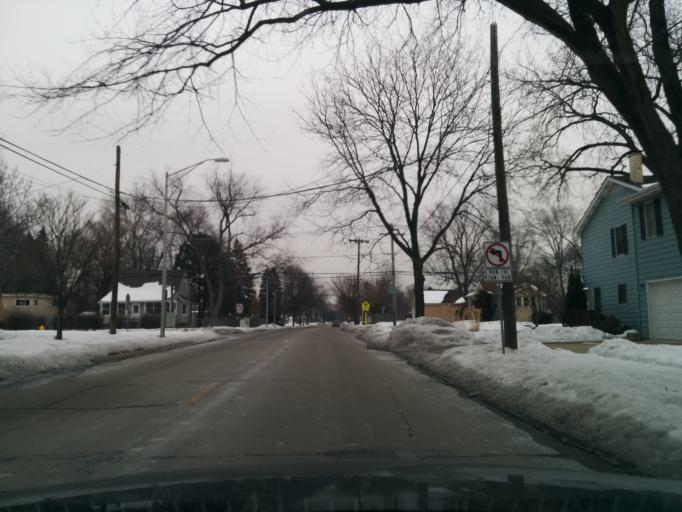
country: US
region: Illinois
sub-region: DuPage County
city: Villa Park
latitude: 41.8845
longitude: -87.9980
